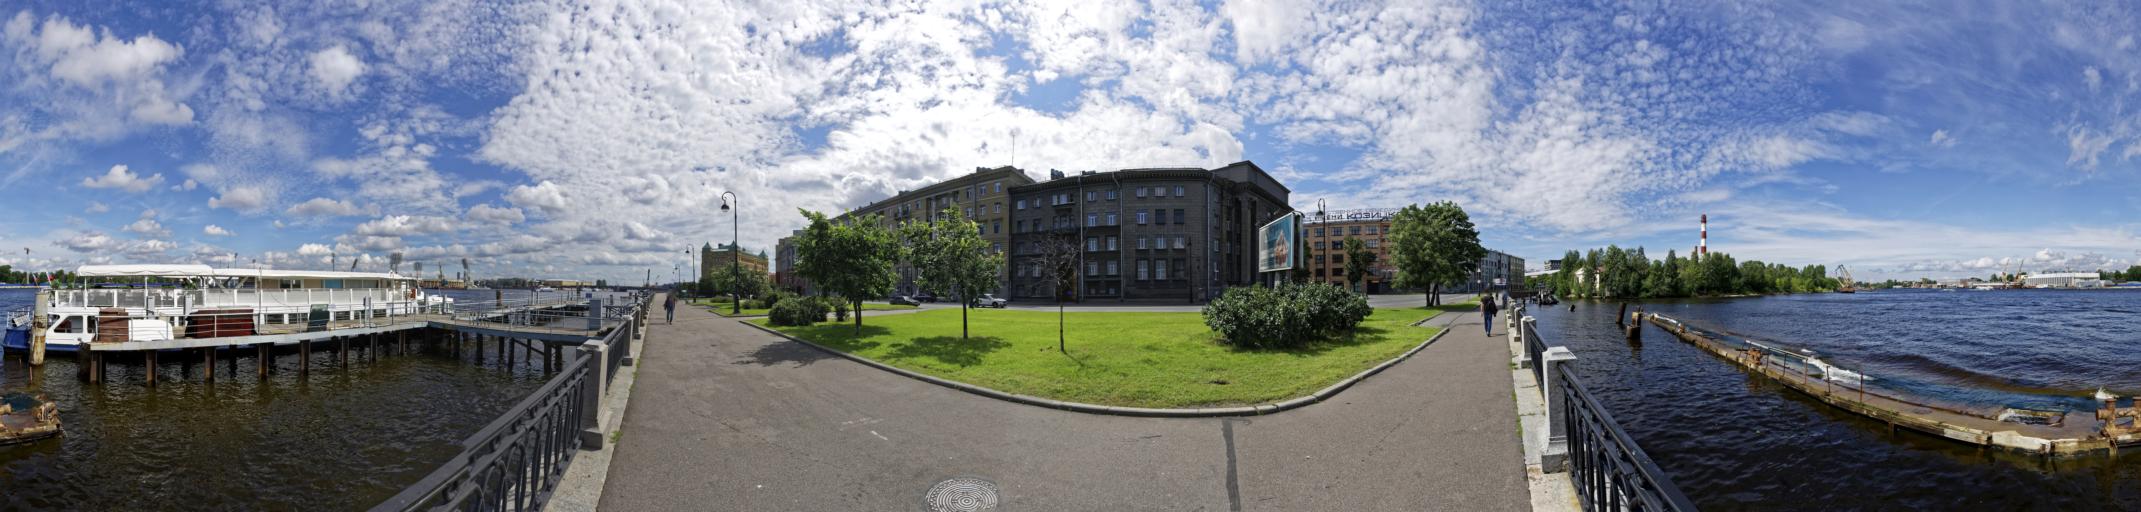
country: RU
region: St.-Petersburg
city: Vasyl'evsky Ostrov
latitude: 59.9501
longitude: 30.2758
